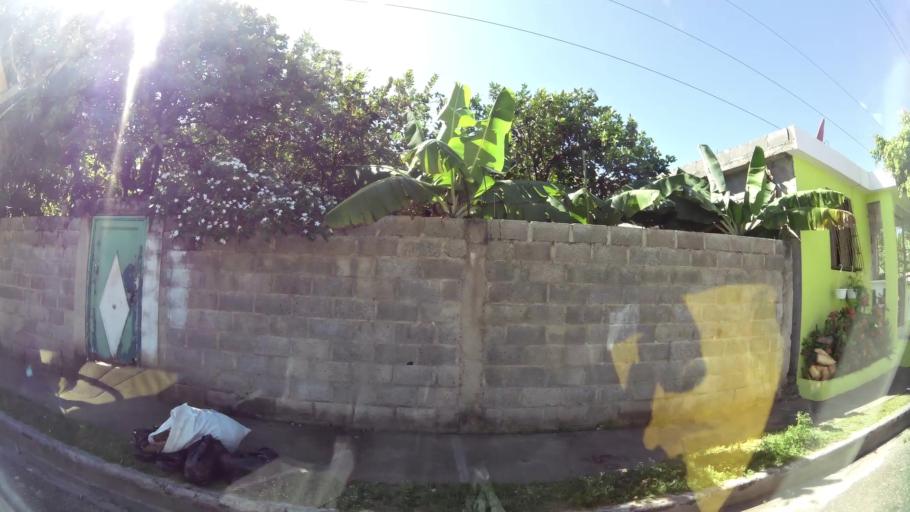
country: DO
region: San Cristobal
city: San Cristobal
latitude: 18.4272
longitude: -70.1244
